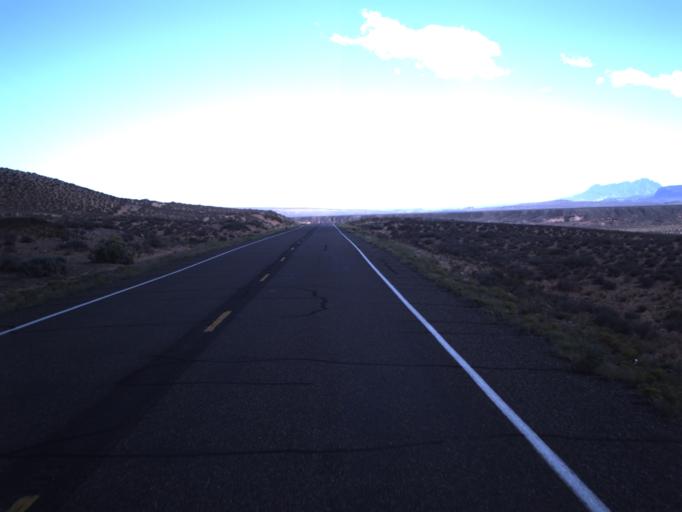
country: US
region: Utah
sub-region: Wayne County
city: Loa
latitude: 38.0807
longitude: -110.6124
